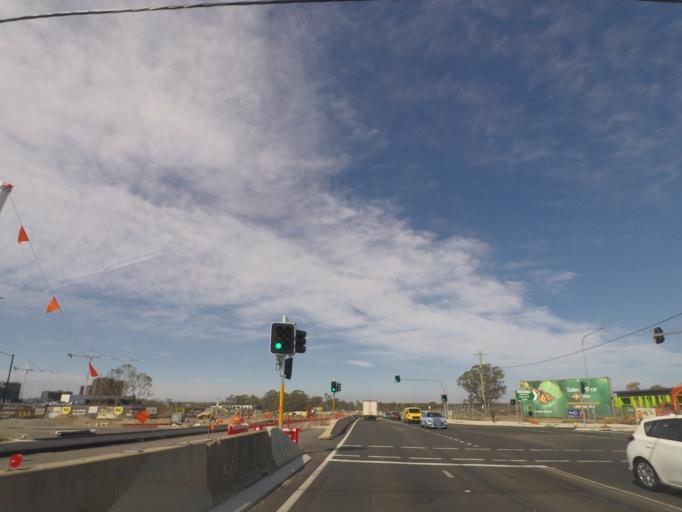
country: AU
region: New South Wales
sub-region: Campbelltown Municipality
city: Denham Court
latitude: -33.9749
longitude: 150.8562
